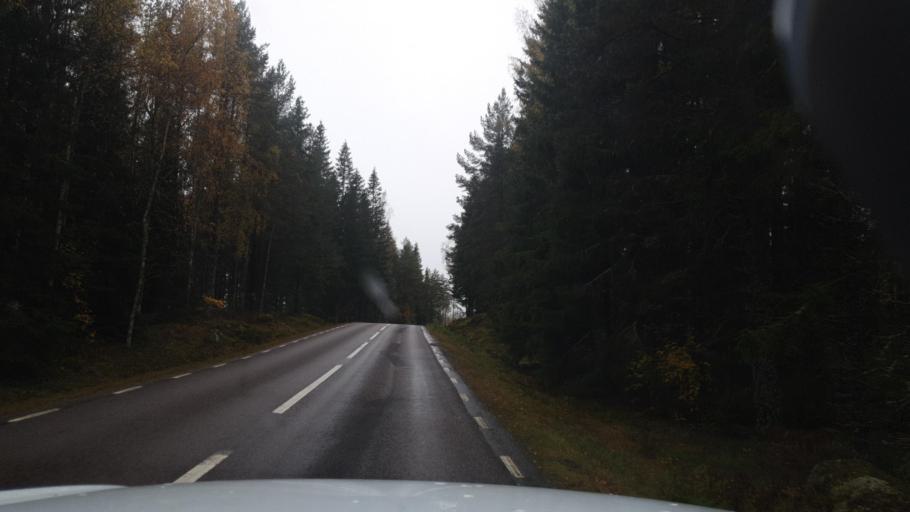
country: SE
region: Vaermland
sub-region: Eda Kommun
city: Amotfors
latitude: 59.6520
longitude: 12.3682
